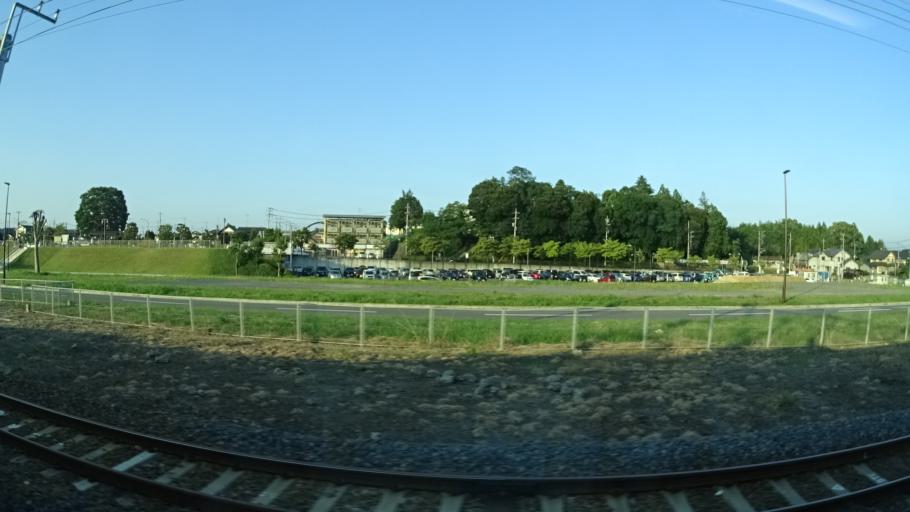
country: JP
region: Ibaraki
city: Ishioka
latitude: 36.1899
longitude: 140.2807
